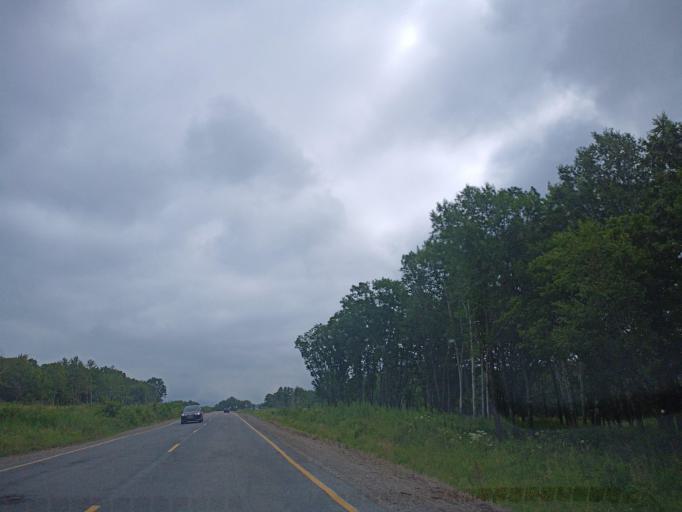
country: RU
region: Primorskiy
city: Dal'nerechensk
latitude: 46.0409
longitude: 133.8932
